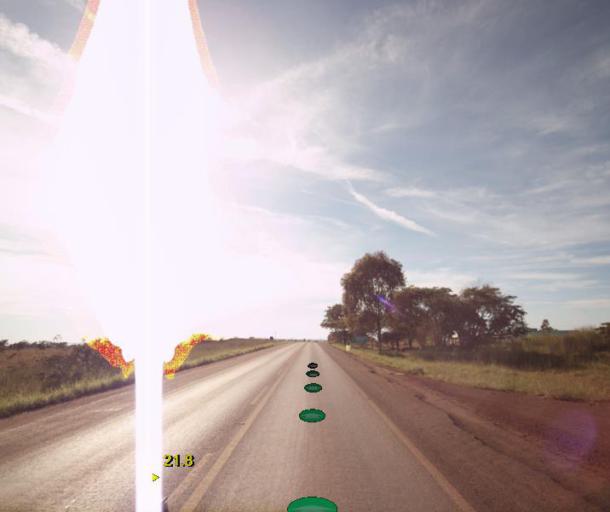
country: BR
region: Federal District
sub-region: Brasilia
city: Brasilia
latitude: -15.7380
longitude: -48.3911
